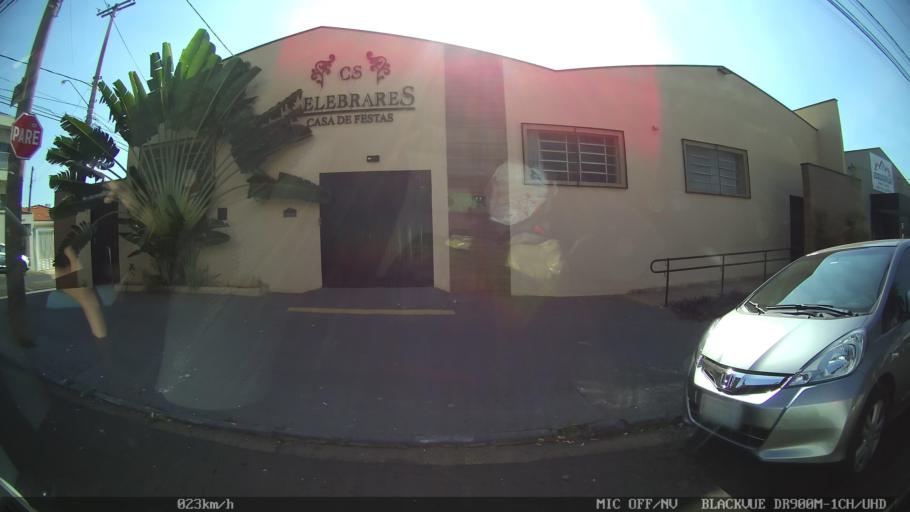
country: BR
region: Sao Paulo
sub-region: Sao Jose Do Rio Preto
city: Sao Jose do Rio Preto
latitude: -20.8009
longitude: -49.3900
